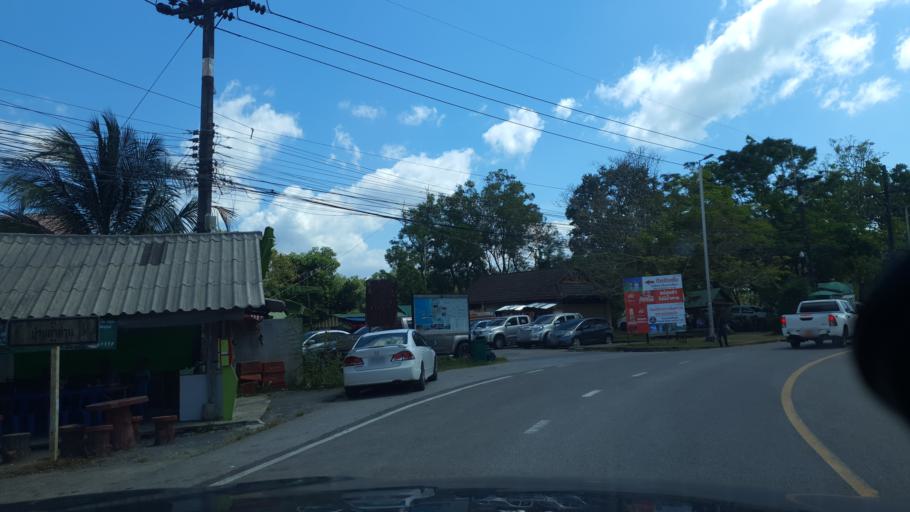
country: TH
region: Phangnga
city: Phang Nga
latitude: 8.4034
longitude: 98.5116
